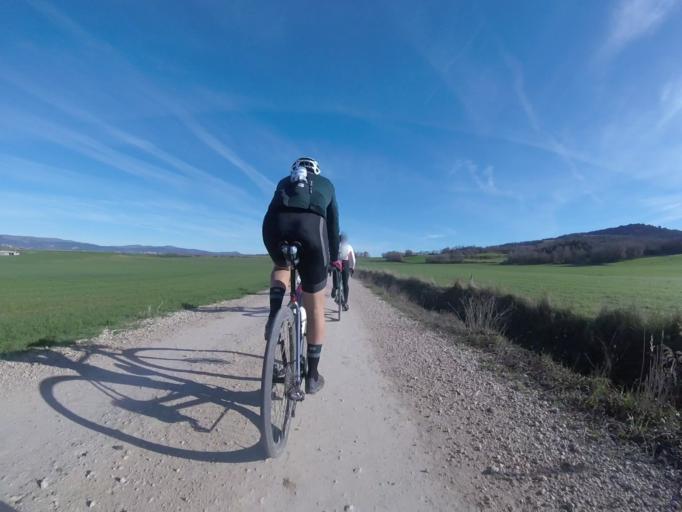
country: ES
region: Navarre
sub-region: Provincia de Navarra
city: Villatuerta
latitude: 42.6531
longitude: -1.9721
